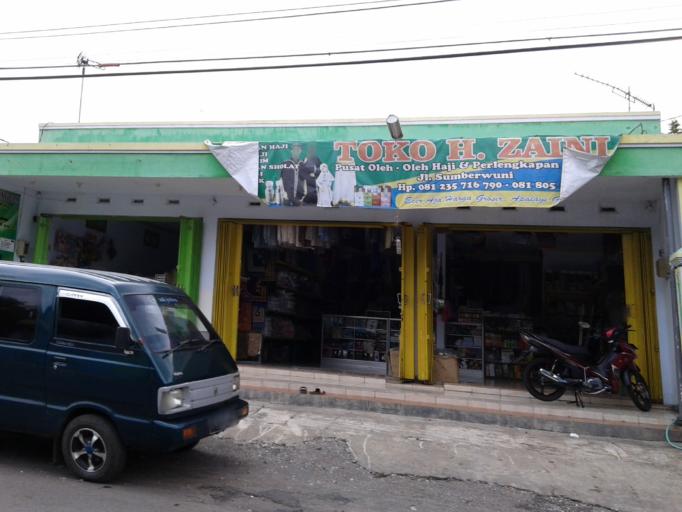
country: ID
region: East Java
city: Lawang
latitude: -7.8446
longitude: 112.6963
